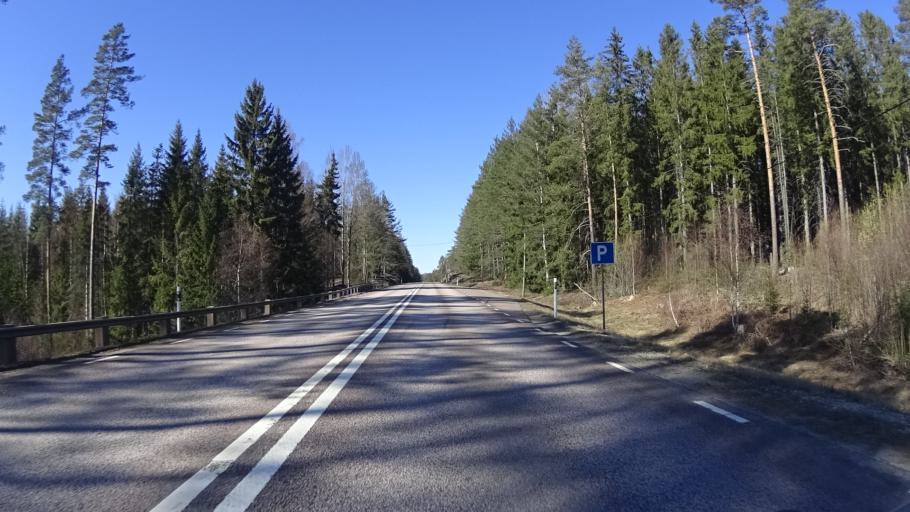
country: SE
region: Vaermland
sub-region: Karlstads Kommun
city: Edsvalla
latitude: 59.5868
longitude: 13.0129
